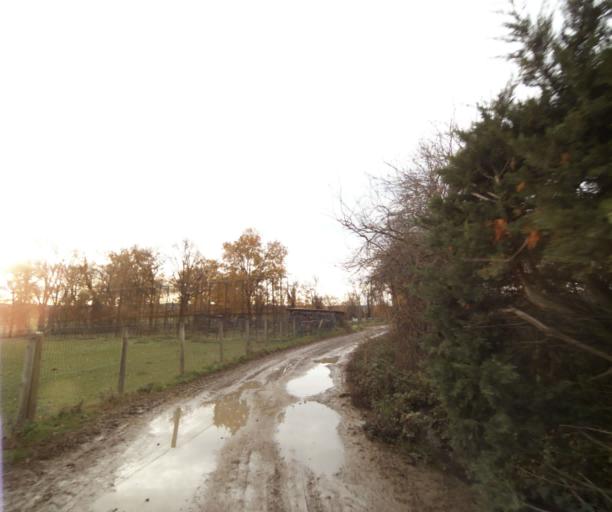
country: FR
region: Rhone-Alpes
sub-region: Departement de la Loire
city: Sury-le-Comtal
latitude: 45.5264
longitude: 4.1643
